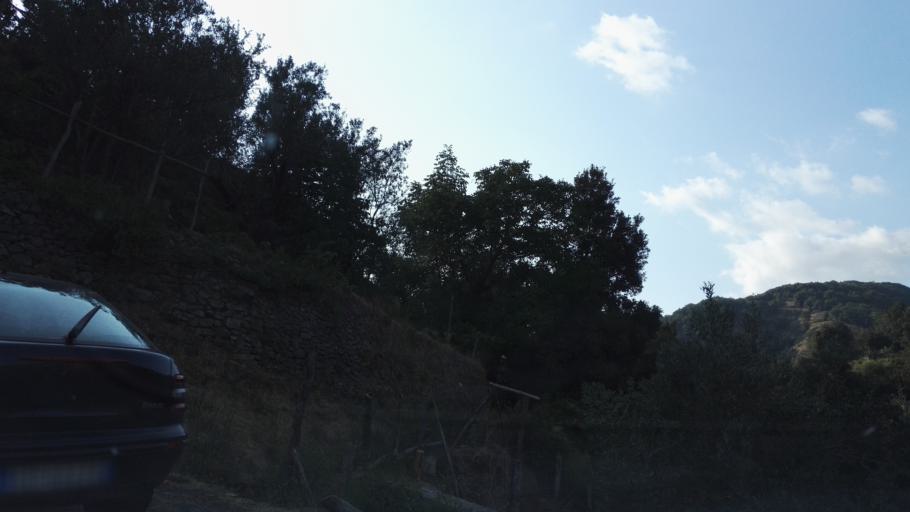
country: IT
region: Calabria
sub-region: Provincia di Vibo-Valentia
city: Nardodipace
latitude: 38.4462
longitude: 16.3407
